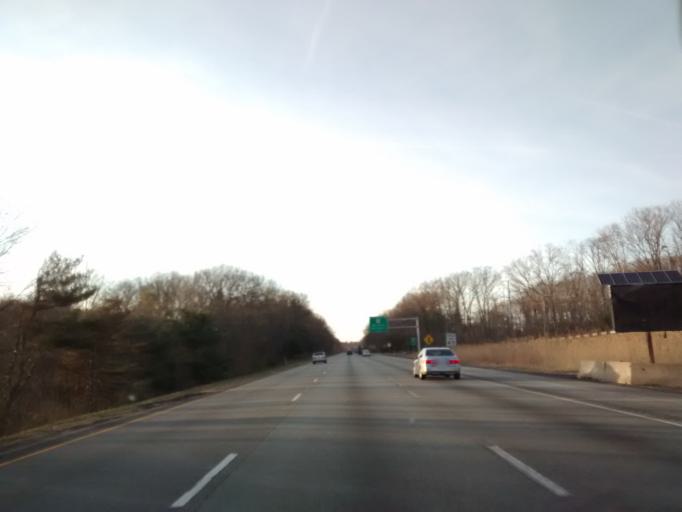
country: US
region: Massachusetts
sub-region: Middlesex County
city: Marlborough
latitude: 42.3223
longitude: -71.5714
